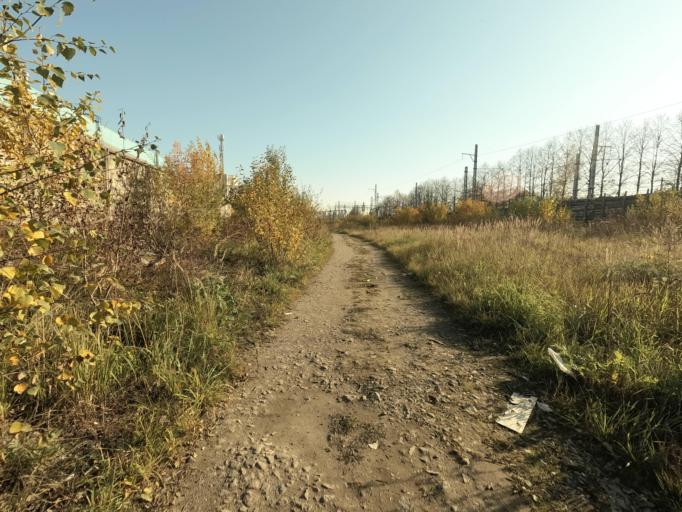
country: RU
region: St.-Petersburg
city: Obukhovo
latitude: 59.8432
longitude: 30.4704
